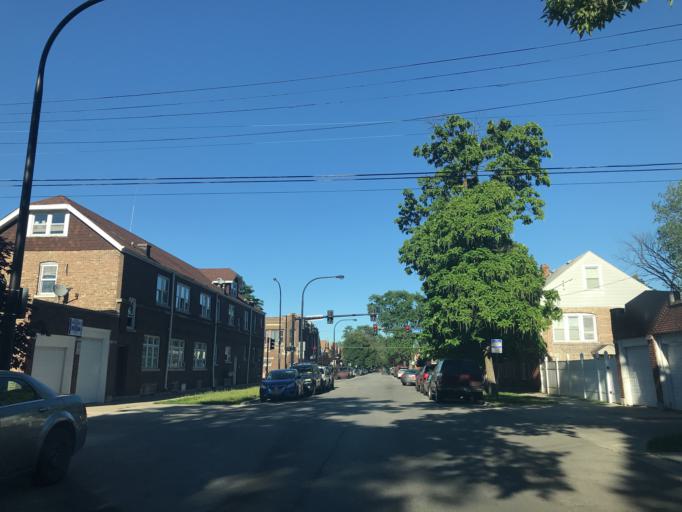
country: US
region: Illinois
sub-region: Cook County
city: Cicero
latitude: 41.8472
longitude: -87.7647
